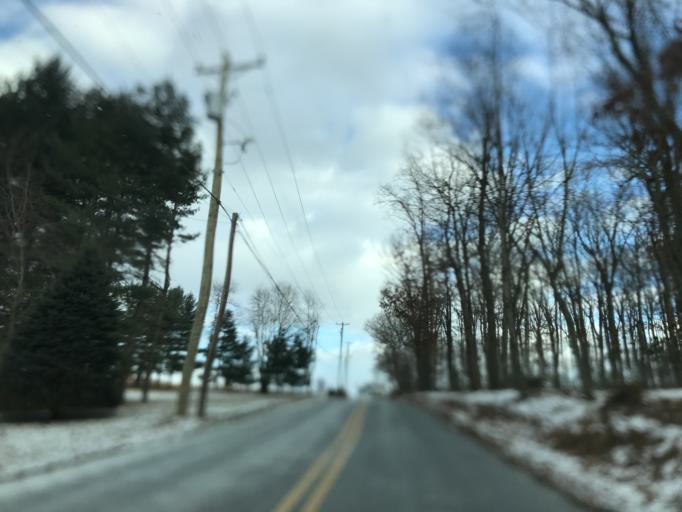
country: US
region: Maryland
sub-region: Harford County
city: Jarrettsville
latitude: 39.6595
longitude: -76.4034
